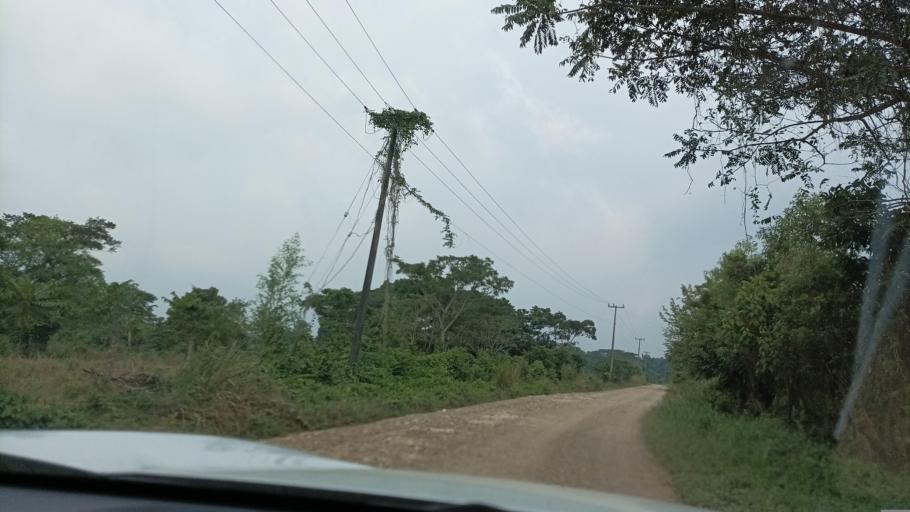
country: MX
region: Veracruz
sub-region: Moloacan
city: Cuichapa
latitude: 17.5843
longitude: -94.2077
